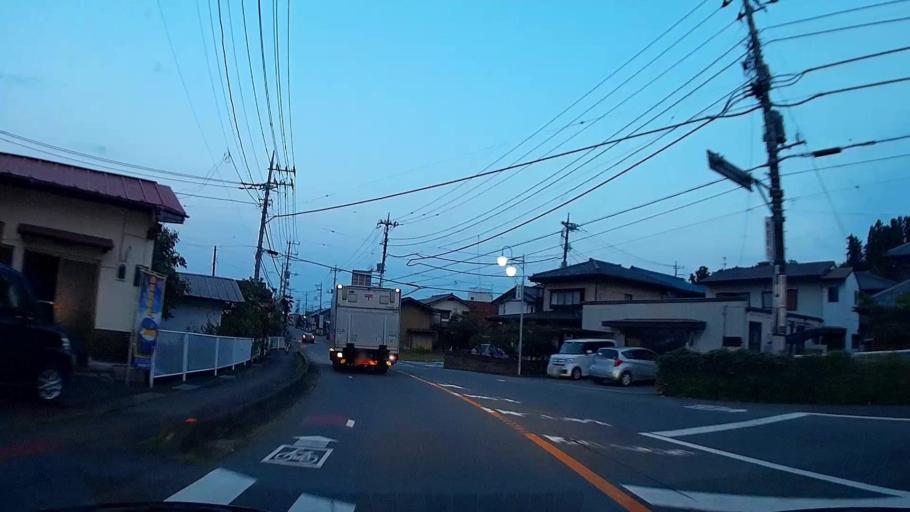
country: JP
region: Gunma
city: Annaka
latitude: 36.3799
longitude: 138.8839
